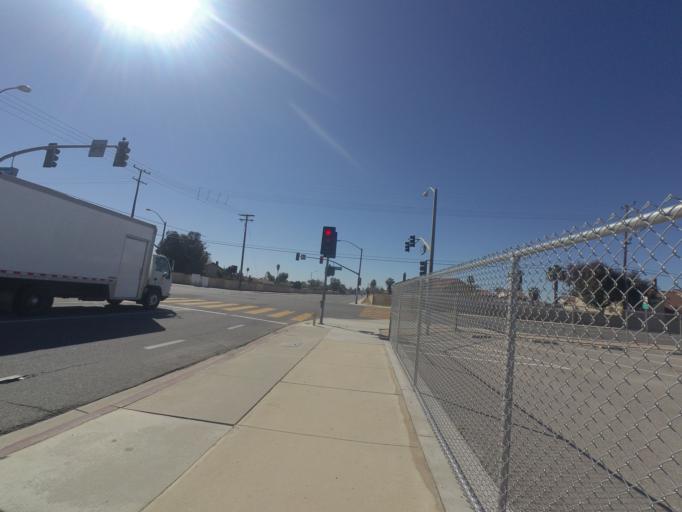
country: US
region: California
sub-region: Riverside County
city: Moreno Valley
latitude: 33.9249
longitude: -117.2526
